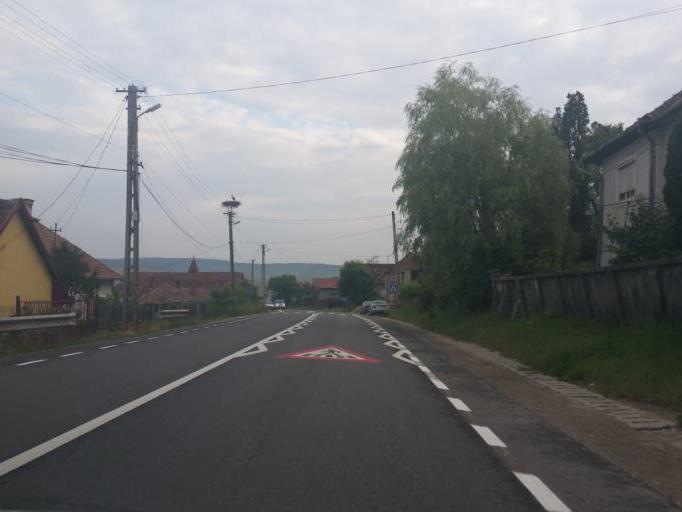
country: RO
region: Cluj
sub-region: Comuna Sanpaul
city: Sanpaul
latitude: 46.9020
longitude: 23.4165
